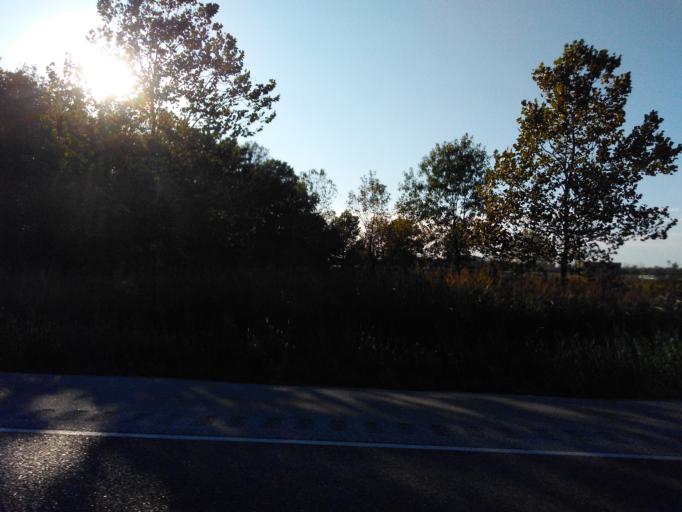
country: US
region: Illinois
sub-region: Saint Clair County
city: Caseyville
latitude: 38.6656
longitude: -90.0297
